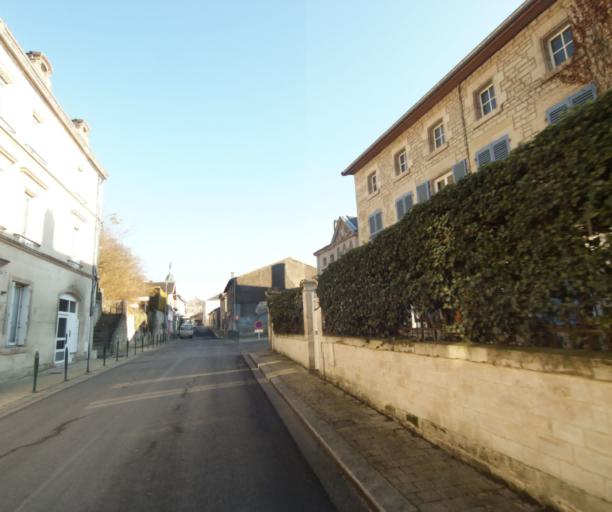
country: FR
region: Champagne-Ardenne
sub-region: Departement de la Haute-Marne
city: Chevillon
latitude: 48.5289
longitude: 5.1309
